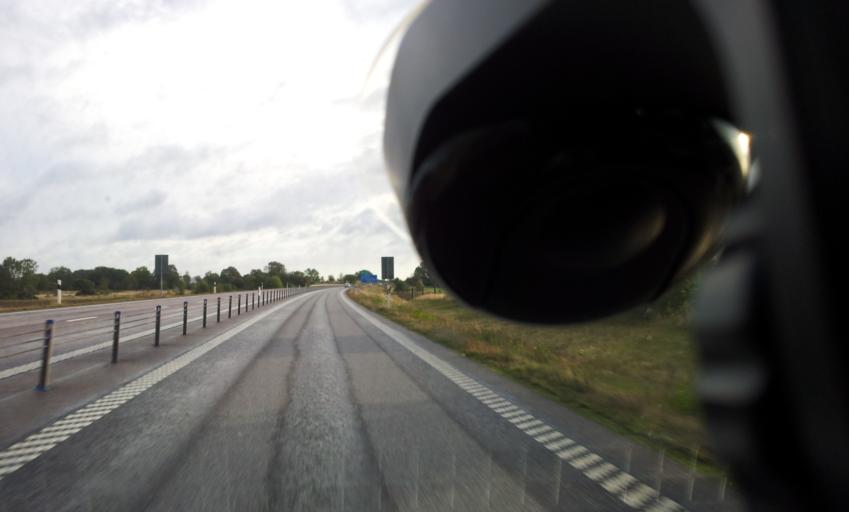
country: SE
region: Kalmar
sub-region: Kalmar Kommun
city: Ljungbyholm
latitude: 56.6136
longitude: 16.1440
